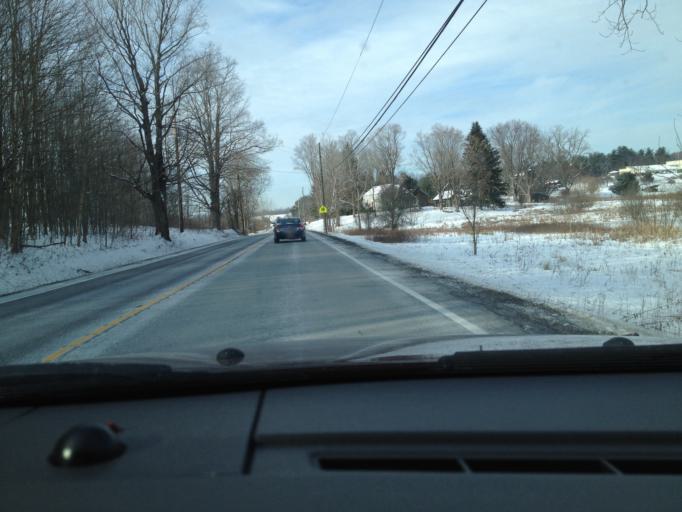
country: US
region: New York
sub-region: Rensselaer County
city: West Sand Lake
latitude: 42.6498
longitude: -73.6485
